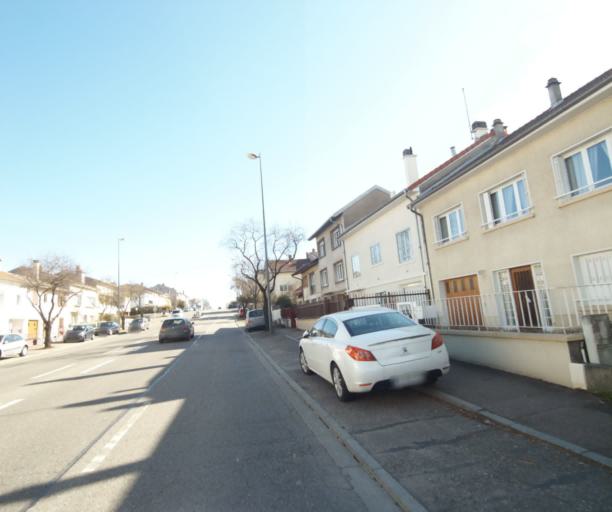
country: FR
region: Lorraine
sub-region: Departement de Meurthe-et-Moselle
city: Villers-les-Nancy
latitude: 48.6759
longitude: 6.1488
